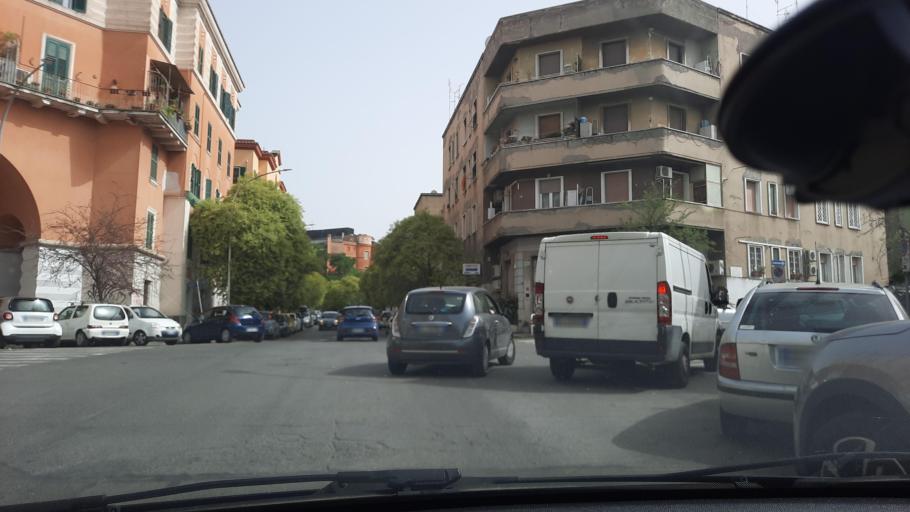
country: IT
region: Latium
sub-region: Citta metropolitana di Roma Capitale
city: Rome
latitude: 41.8622
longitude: 12.4933
